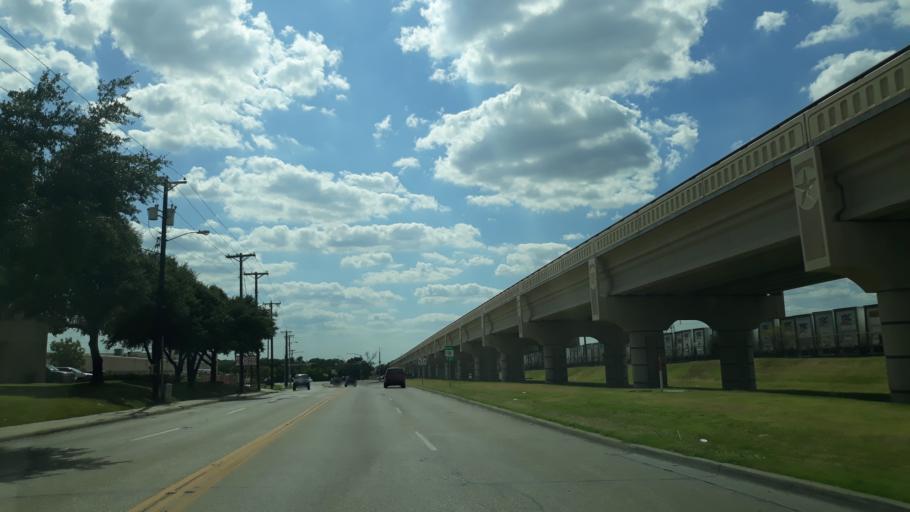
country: US
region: Texas
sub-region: Dallas County
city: Irving
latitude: 32.8155
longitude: -96.9913
